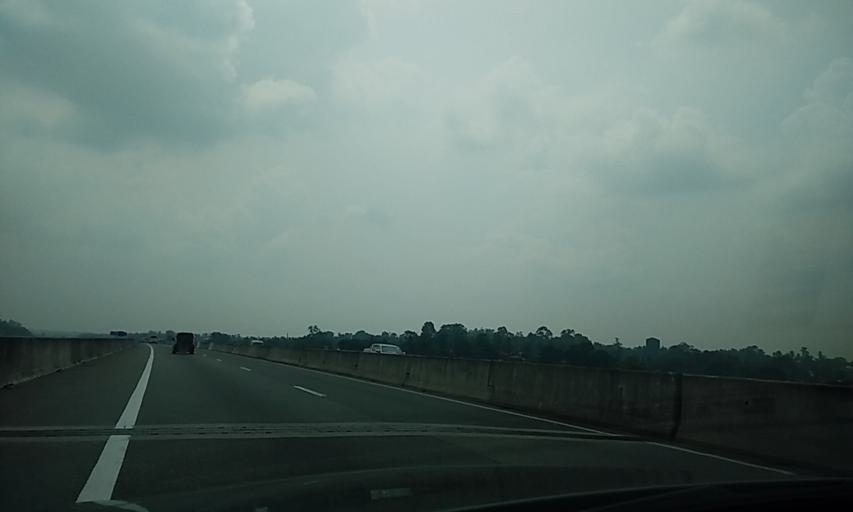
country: LK
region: Western
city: Mulleriyawa
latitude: 6.9101
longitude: 79.9814
